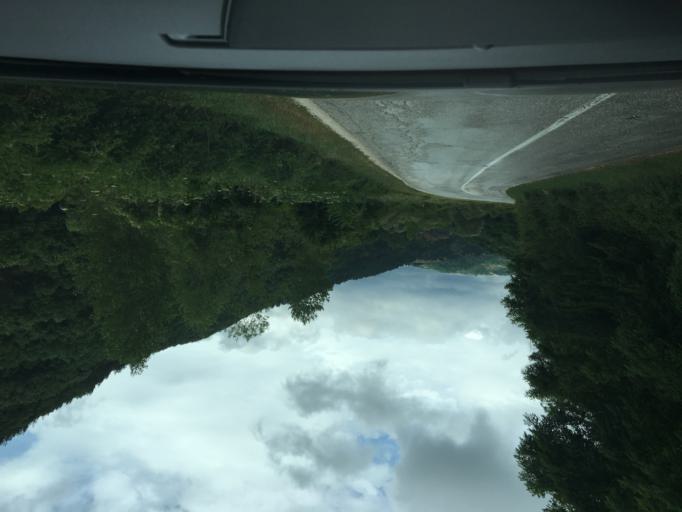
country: MK
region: Kriva Palanka
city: Kriva Palanka
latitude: 42.2260
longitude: 22.3876
